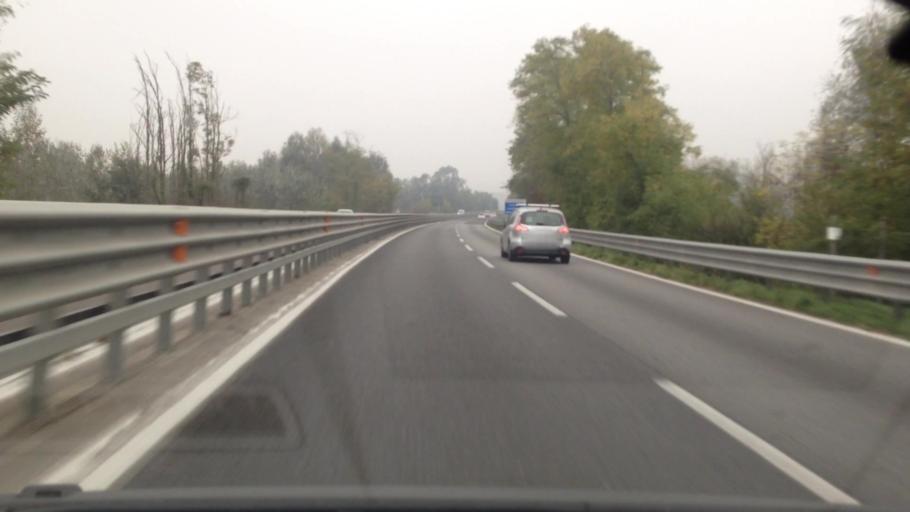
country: IT
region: Piedmont
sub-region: Provincia di Asti
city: Azzano d'Asti
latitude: 44.9006
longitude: 8.2462
